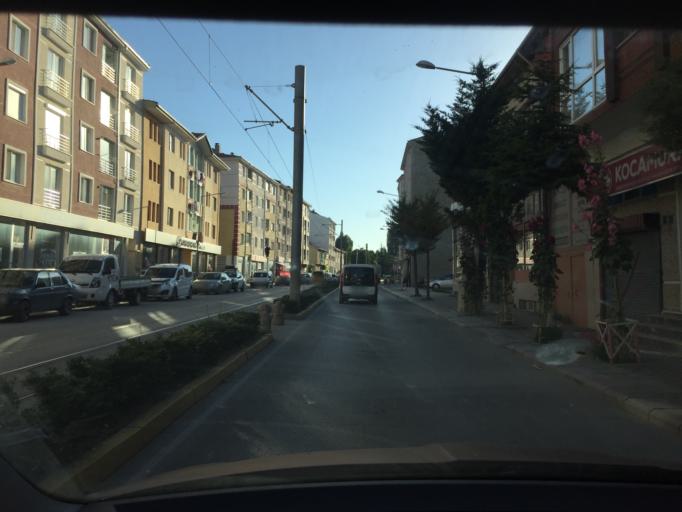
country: TR
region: Eskisehir
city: Eskisehir
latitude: 39.7749
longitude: 30.4606
